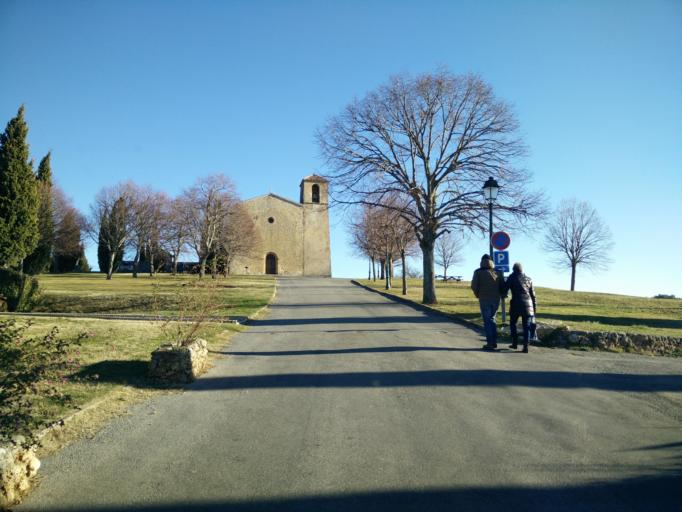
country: FR
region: Provence-Alpes-Cote d'Azur
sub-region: Departement du Var
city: Villecroze
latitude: 43.5886
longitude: 6.3037
